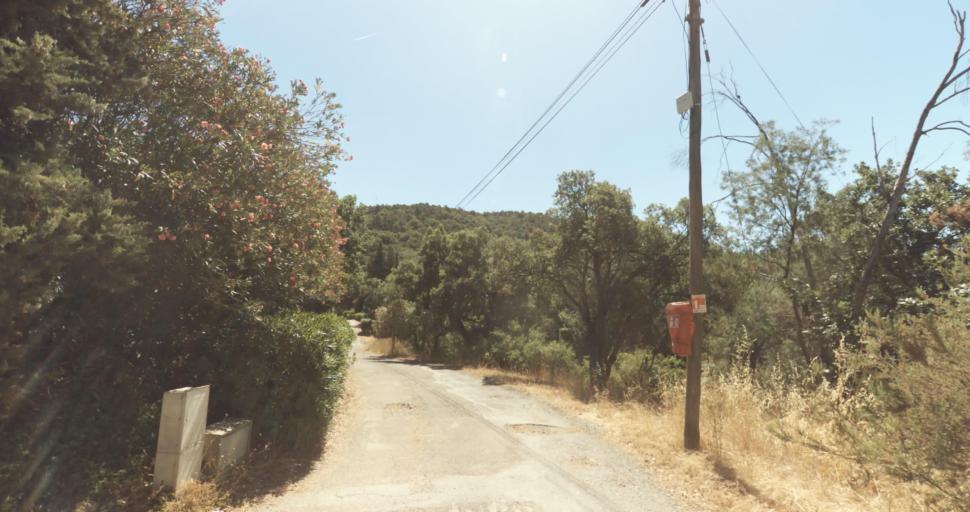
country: FR
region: Provence-Alpes-Cote d'Azur
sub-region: Departement du Var
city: Gassin
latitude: 43.2383
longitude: 6.5778
